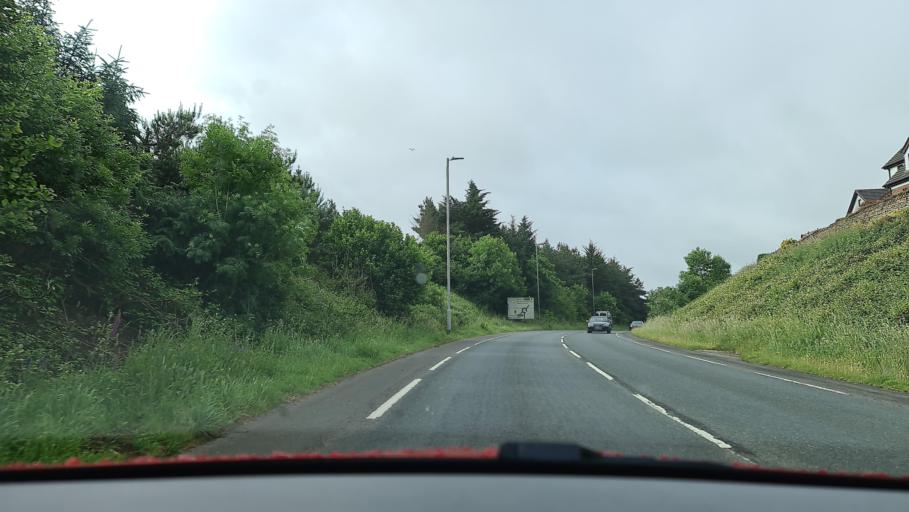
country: GB
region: England
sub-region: Cornwall
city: Liskeard
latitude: 50.4531
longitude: -4.4493
